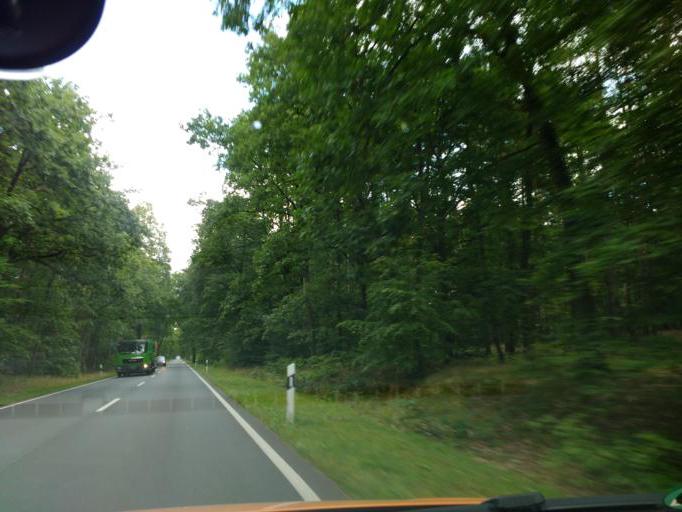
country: DE
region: Brandenburg
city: Marienwerder
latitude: 52.8372
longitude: 13.5076
